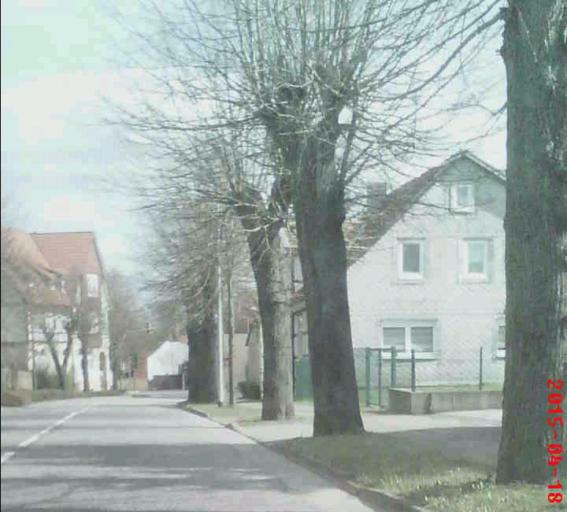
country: DE
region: Thuringia
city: Worbis
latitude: 51.4254
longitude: 10.3553
